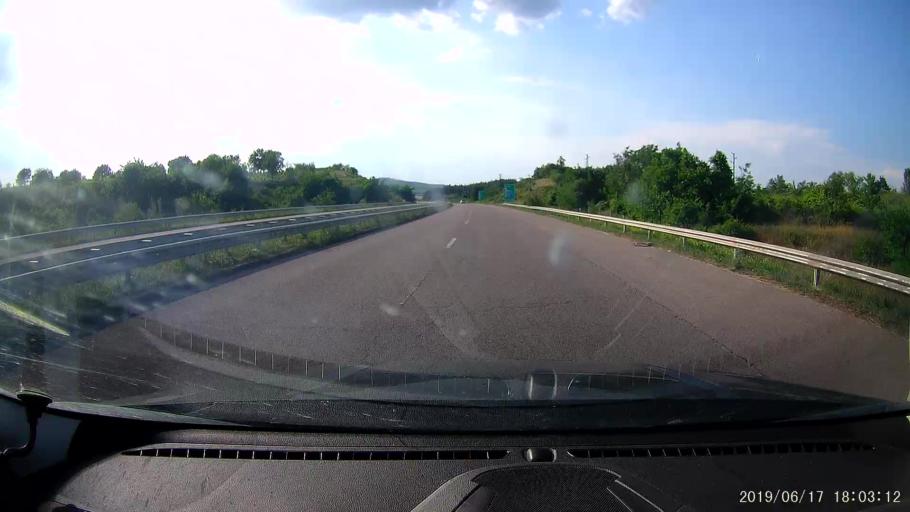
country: BG
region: Khaskovo
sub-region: Obshtina Svilengrad
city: Svilengrad
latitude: 41.7736
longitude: 26.2234
